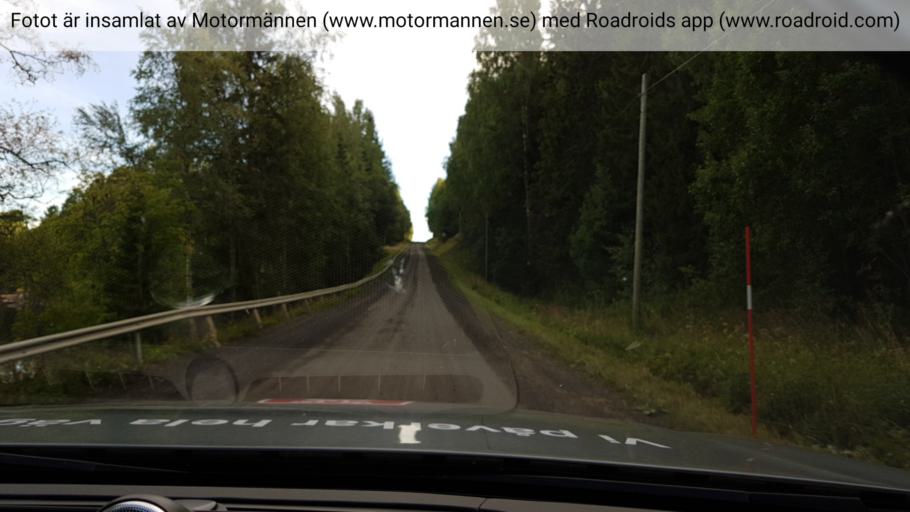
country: SE
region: Jaemtland
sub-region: Stroemsunds Kommun
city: Stroemsund
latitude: 64.0933
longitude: 15.8254
